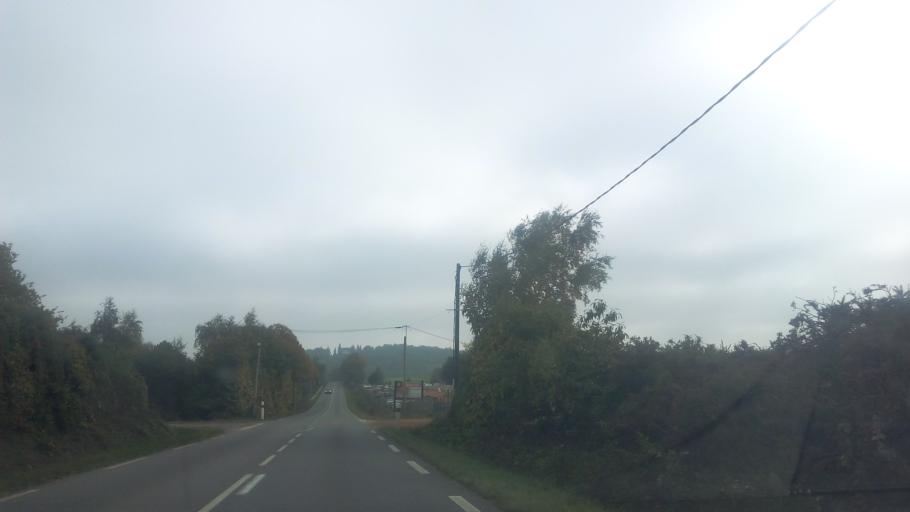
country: FR
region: Pays de la Loire
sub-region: Departement de la Loire-Atlantique
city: Guemene-Penfao
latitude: 47.6354
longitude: -1.9066
